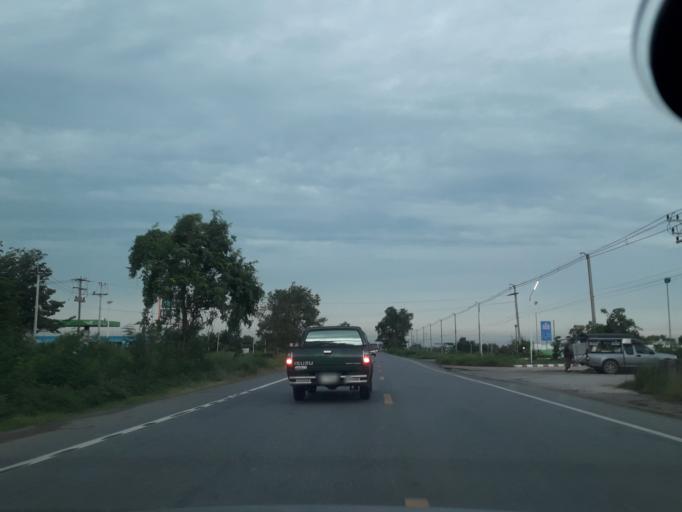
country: TH
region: Phra Nakhon Si Ayutthaya
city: Wang Noi
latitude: 14.1639
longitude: 100.7474
